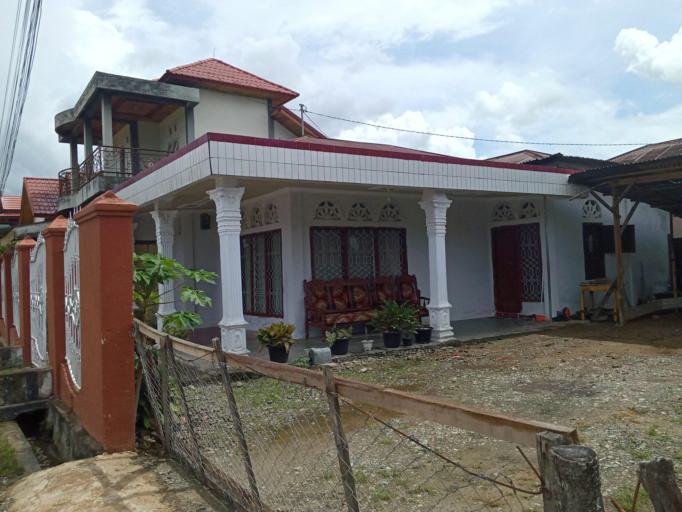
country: ID
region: Jambi
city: Semurup
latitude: -1.9895
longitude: 101.3693
